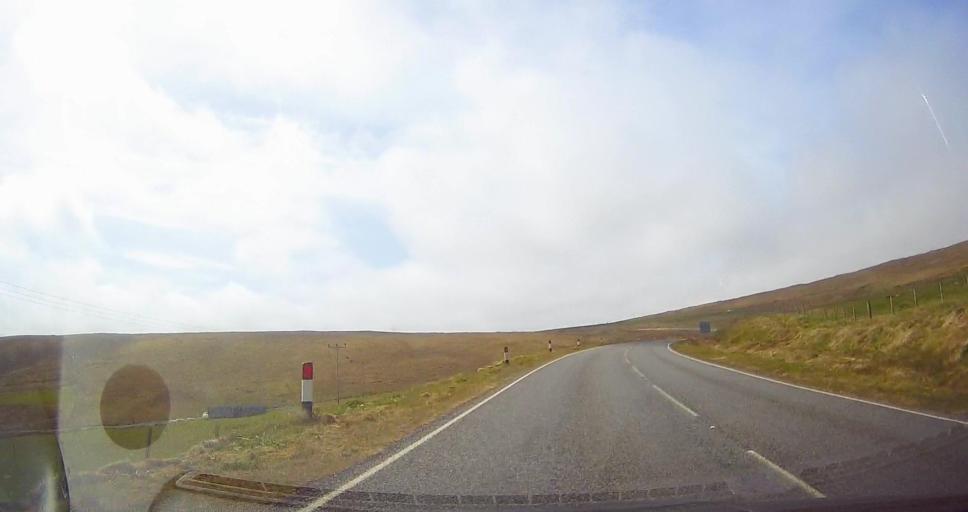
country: GB
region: Scotland
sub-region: Shetland Islands
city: Sandwick
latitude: 60.0090
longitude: -1.2506
